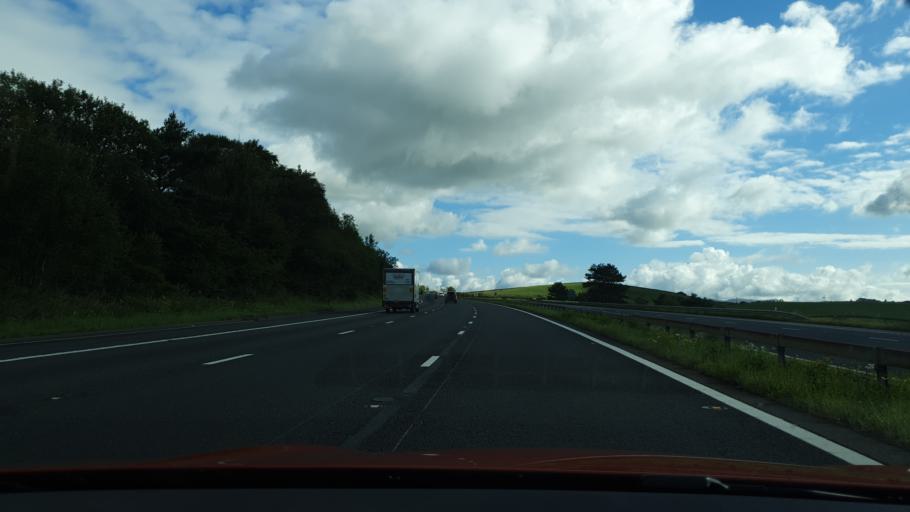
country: GB
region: England
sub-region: Cumbria
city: Kendal
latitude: 54.2932
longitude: -2.6561
